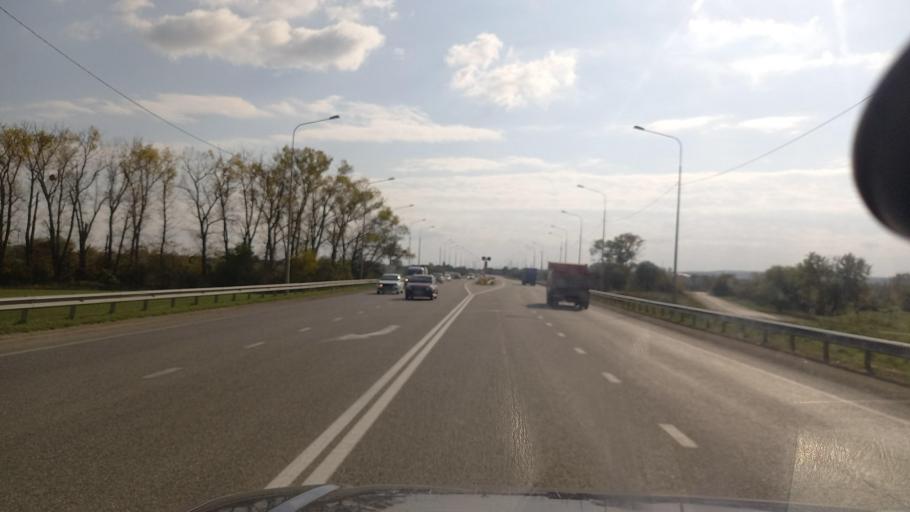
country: RU
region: Krasnodarskiy
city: Novoukrainskiy
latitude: 44.9015
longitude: 38.0362
